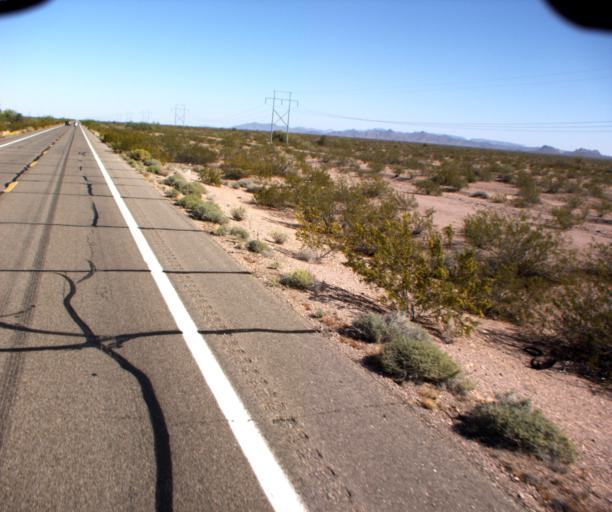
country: US
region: Arizona
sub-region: La Paz County
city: Quartzsite
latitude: 33.3469
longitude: -114.2170
